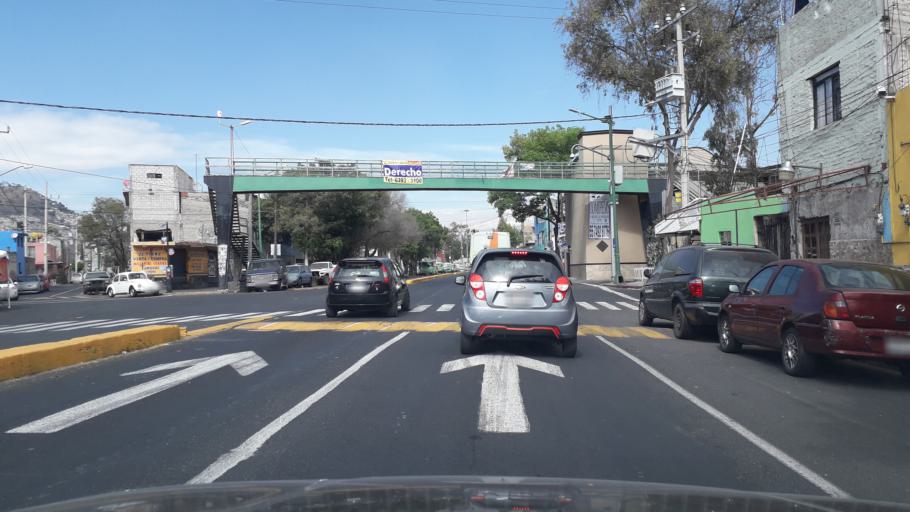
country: MX
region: Mexico City
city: Gustavo A. Madero
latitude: 19.5038
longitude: -99.0909
